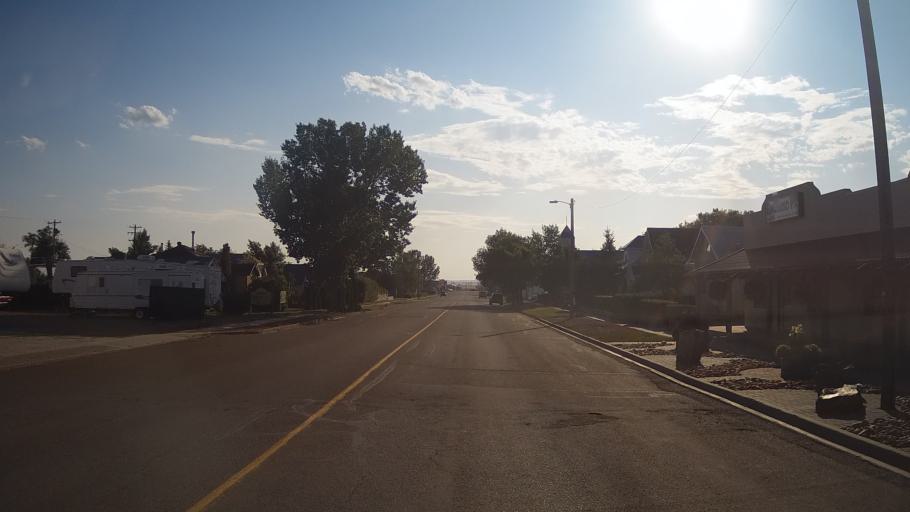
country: CA
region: Alberta
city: Hanna
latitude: 51.6419
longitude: -111.9329
